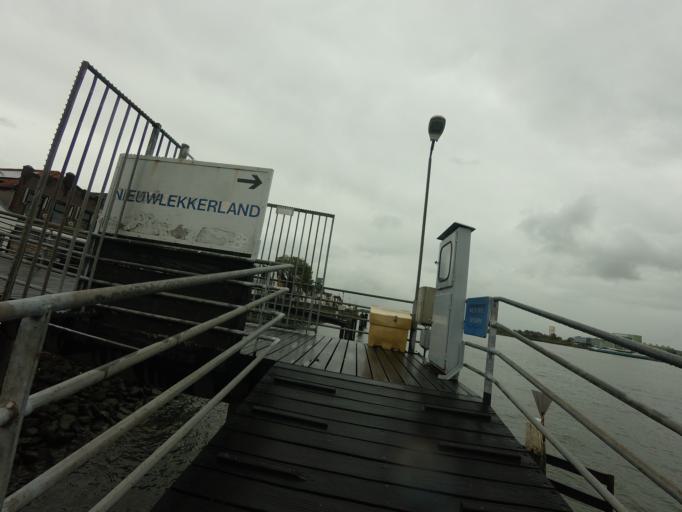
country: NL
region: South Holland
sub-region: Molenwaard
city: Nieuw-Lekkerland
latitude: 51.8946
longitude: 4.6842
